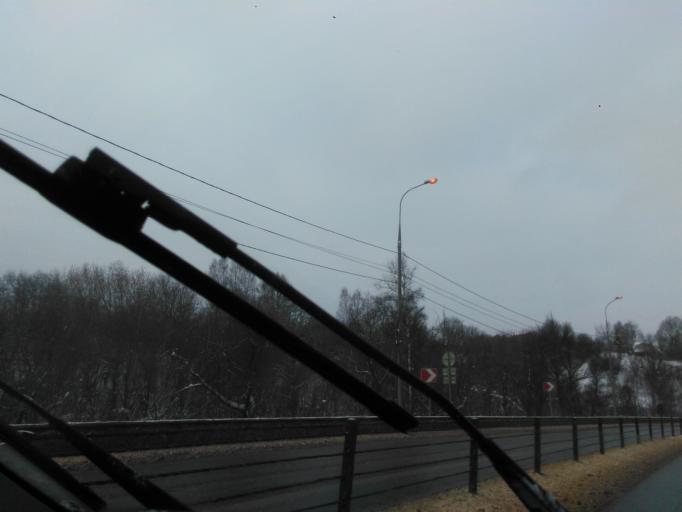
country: RU
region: Moskovskaya
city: Dedenevo
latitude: 56.2517
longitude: 37.5139
